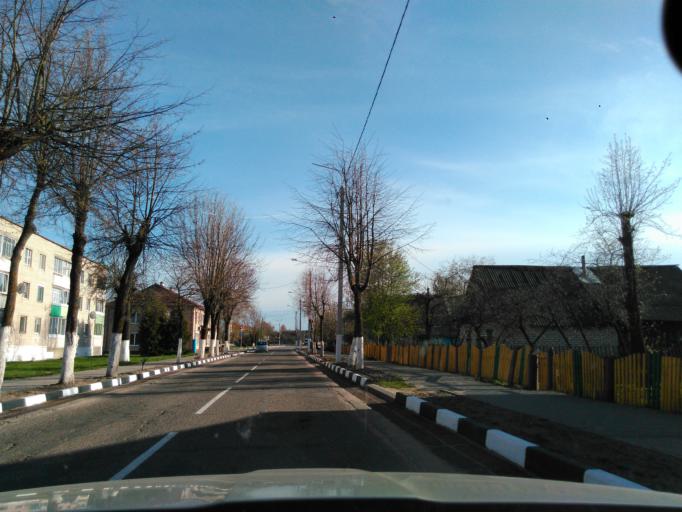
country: BY
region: Vitebsk
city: Chashniki
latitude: 54.8590
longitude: 29.1604
